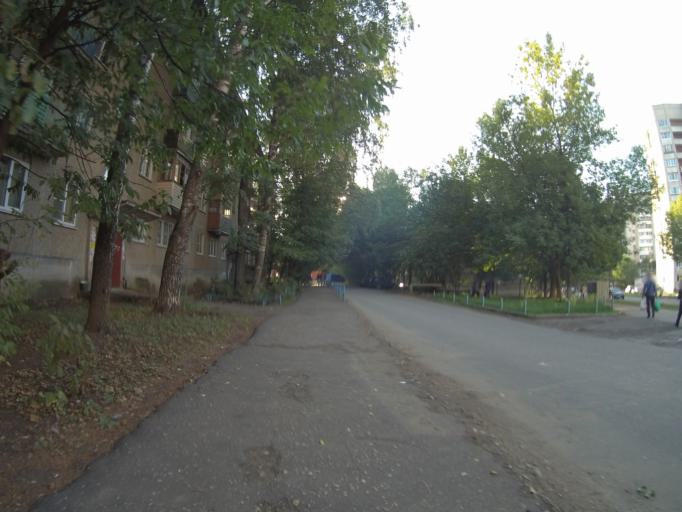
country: RU
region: Vladimir
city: Vladimir
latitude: 56.1475
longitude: 40.3673
